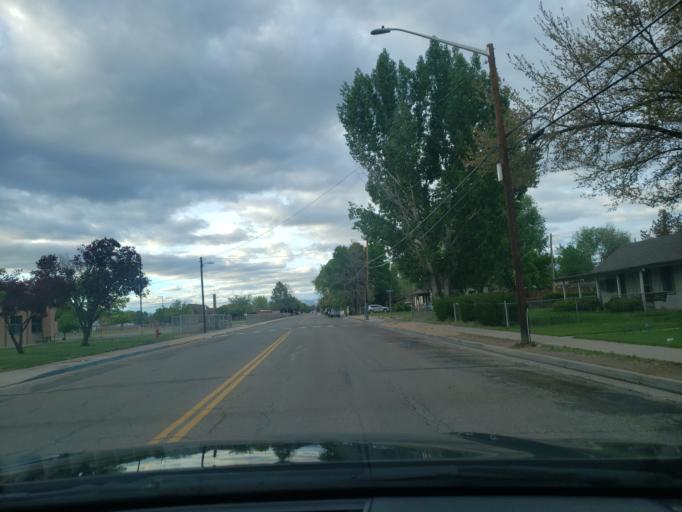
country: US
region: Colorado
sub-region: Mesa County
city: Fruita
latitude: 39.1621
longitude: -108.7290
